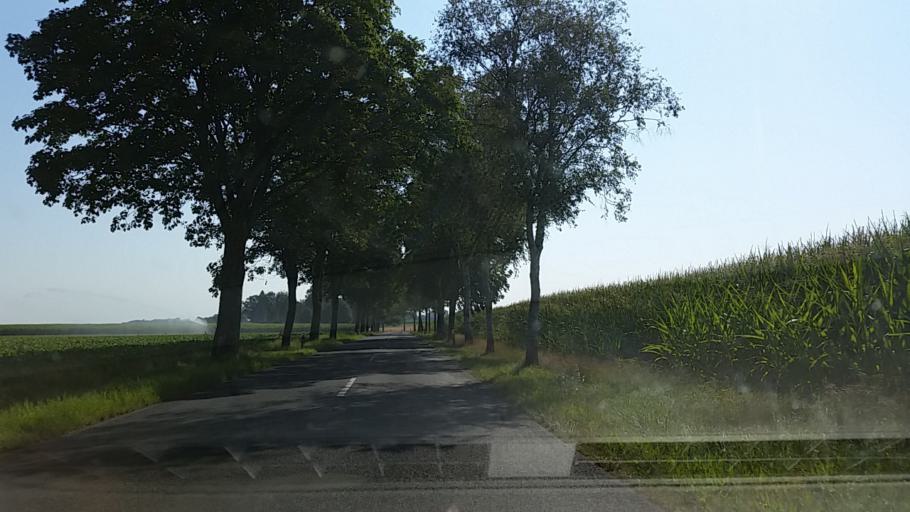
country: DE
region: Lower Saxony
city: Luder
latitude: 52.8103
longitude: 10.6413
